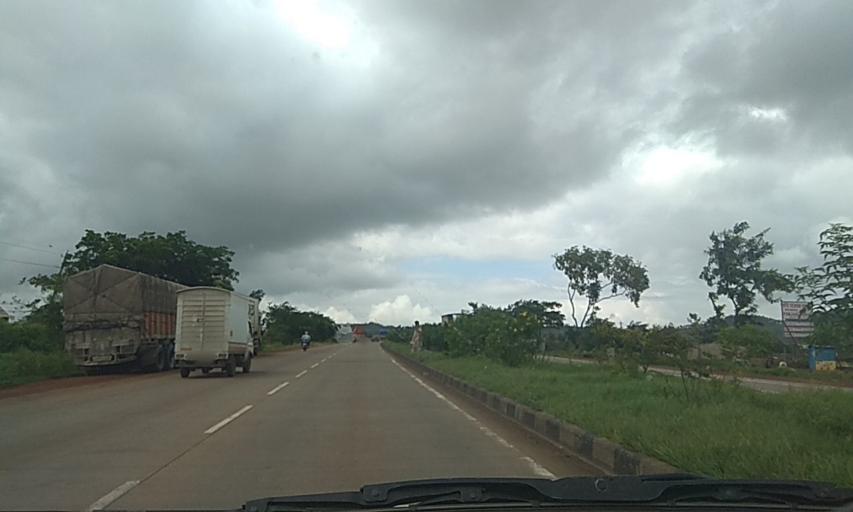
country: IN
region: Karnataka
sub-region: Belgaum
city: Sankeshwar
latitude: 16.2587
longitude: 74.4680
